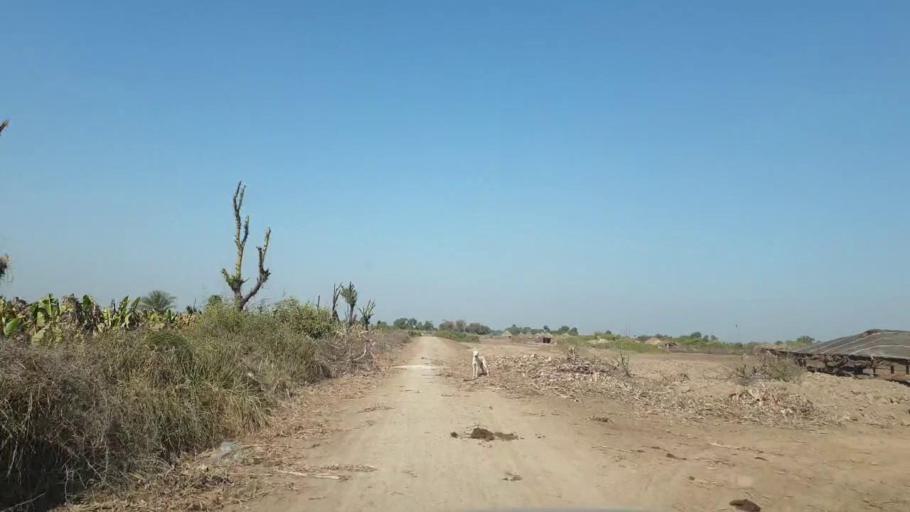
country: PK
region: Sindh
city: Tando Adam
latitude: 25.6463
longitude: 68.6863
